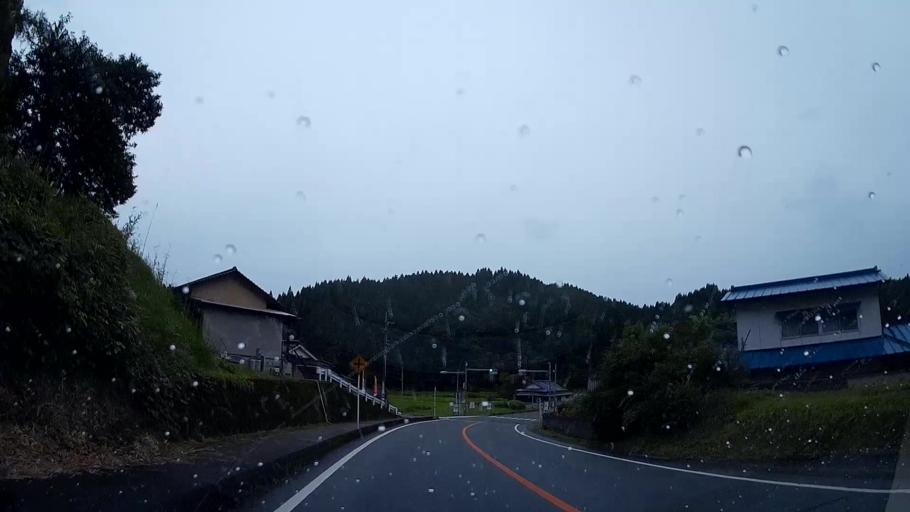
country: JP
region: Oita
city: Tsukawaki
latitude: 33.1287
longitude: 131.0859
